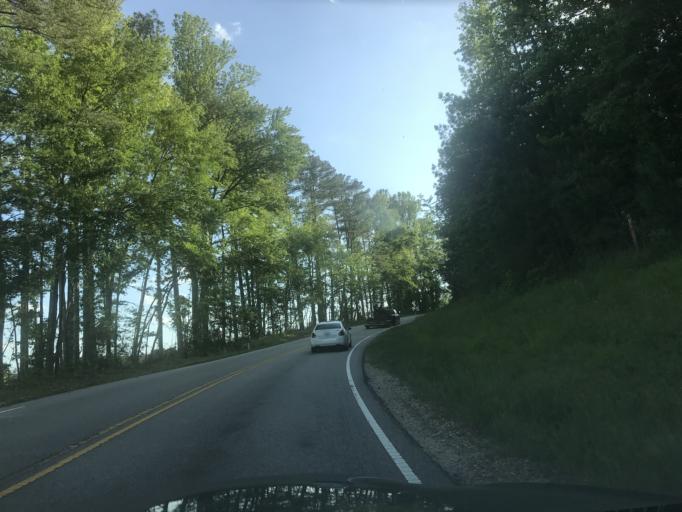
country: US
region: North Carolina
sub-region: Wake County
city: Knightdale
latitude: 35.7511
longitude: -78.4299
